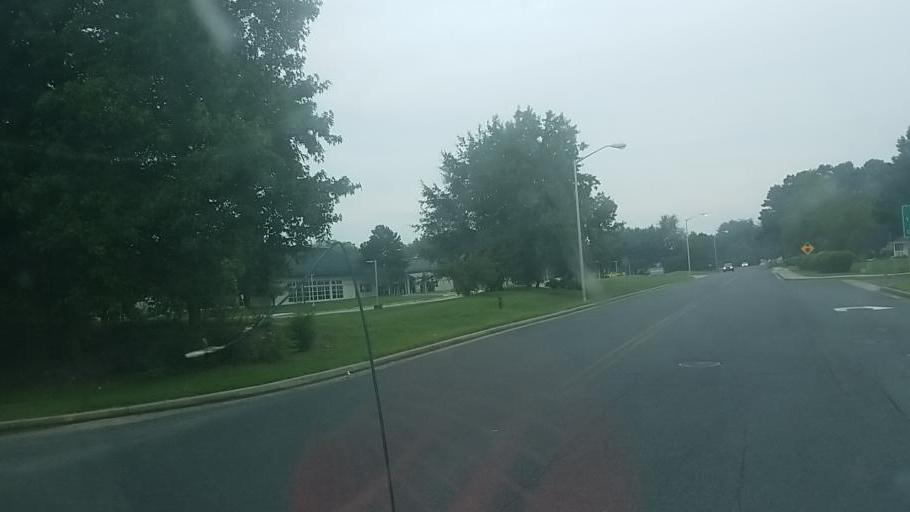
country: US
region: Maryland
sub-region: Wicomico County
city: Salisbury
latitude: 38.3681
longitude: -75.5476
